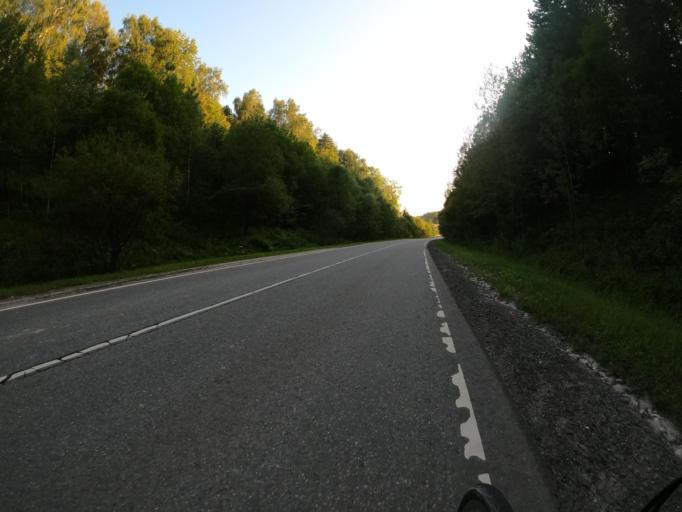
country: RU
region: Moskovskaya
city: Meshcherino
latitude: 55.1080
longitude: 38.3039
